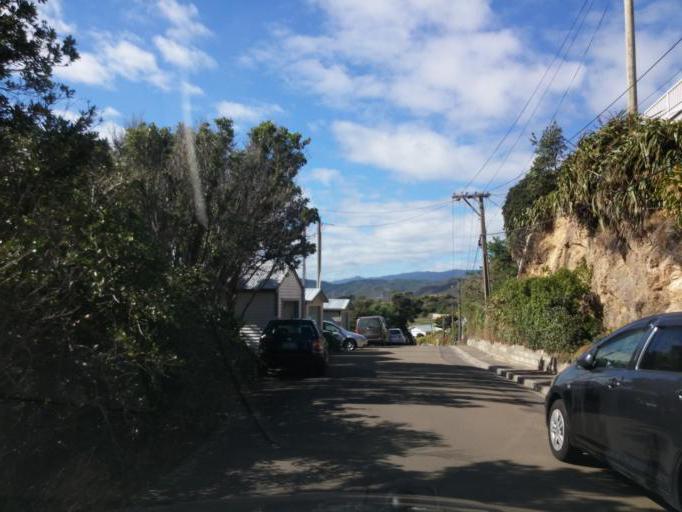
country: NZ
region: Wellington
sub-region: Wellington City
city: Wellington
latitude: -41.3284
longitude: 174.8333
